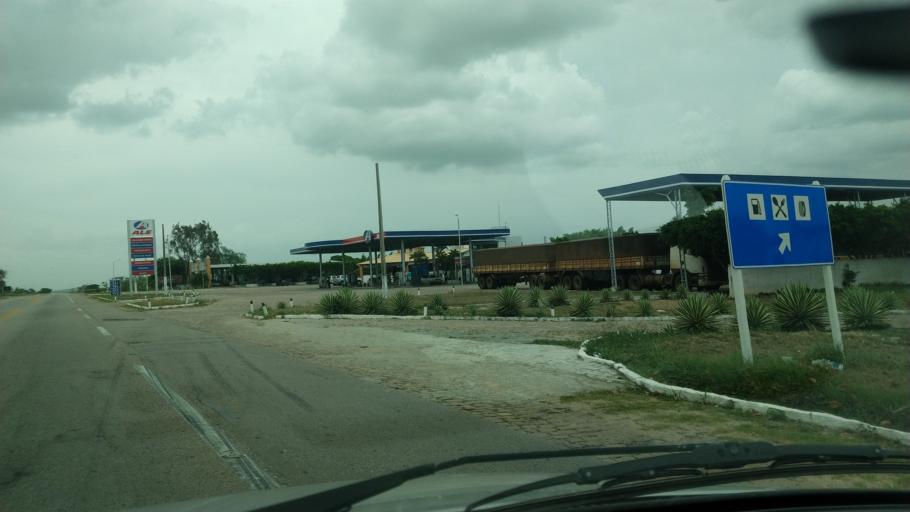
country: BR
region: Rio Grande do Norte
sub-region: Tangara
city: Tangara
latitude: -6.1728
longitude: -35.7642
